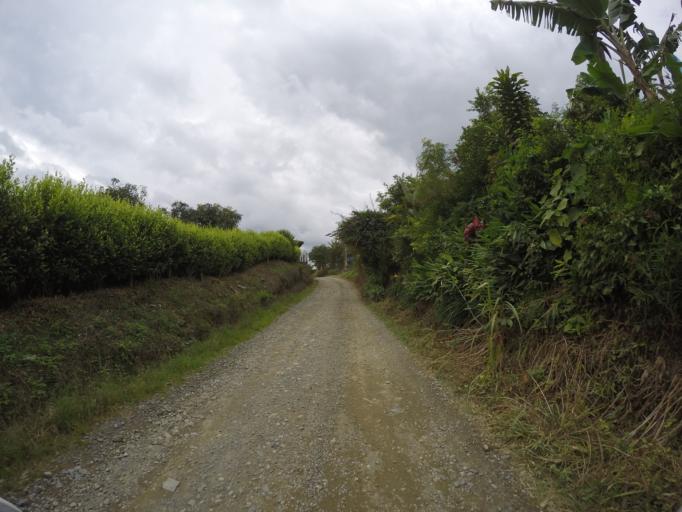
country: CO
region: Quindio
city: Circasia
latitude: 4.6267
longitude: -75.6864
